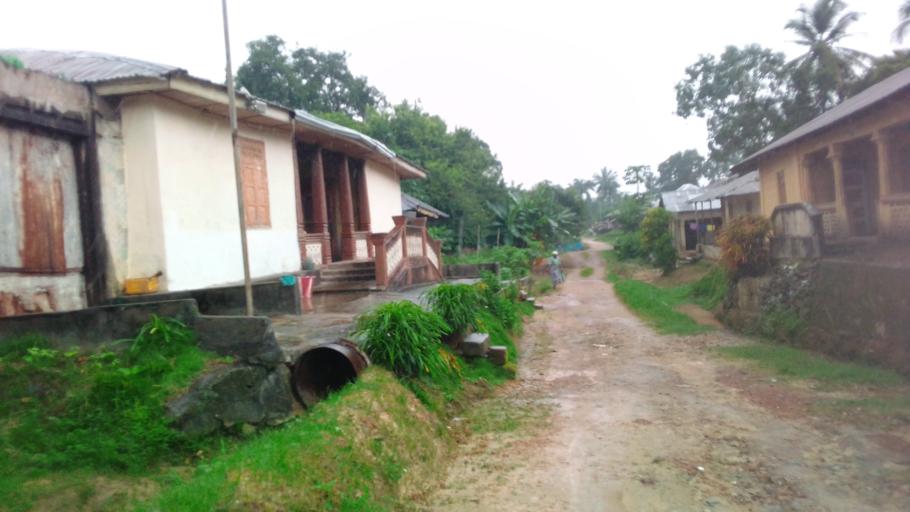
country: SL
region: Northern Province
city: Lunsar
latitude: 8.6808
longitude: -12.5292
